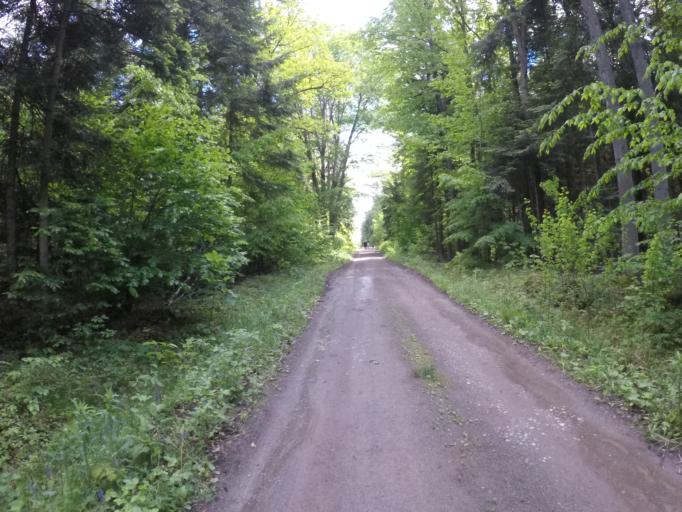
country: PL
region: Swietokrzyskie
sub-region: Powiat kielecki
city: Kostomloty Pierwsze
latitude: 50.9203
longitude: 20.6339
